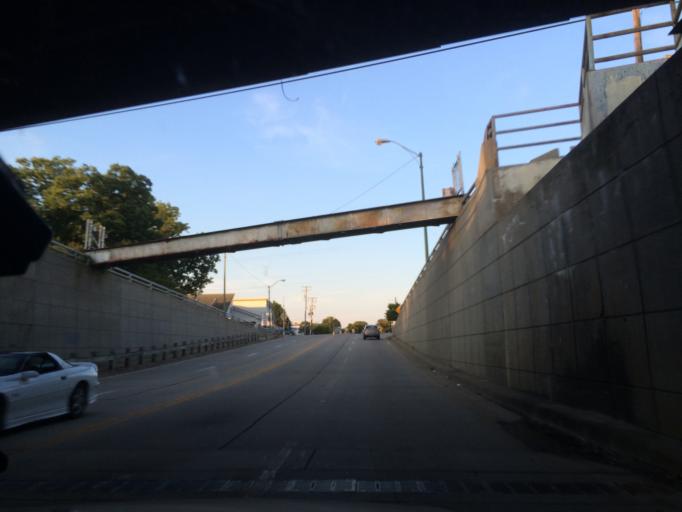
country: US
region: Virginia
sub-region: City of Newport News
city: Newport News
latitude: 37.0342
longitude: -76.4589
